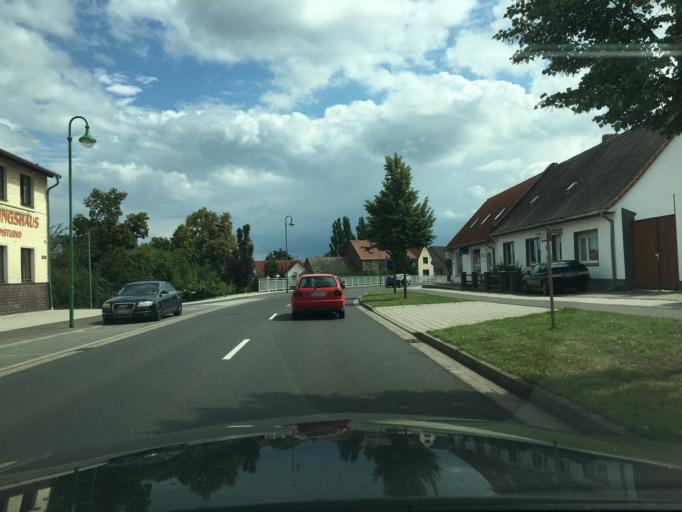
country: DE
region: Saxony-Anhalt
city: Bobbau
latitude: 51.6892
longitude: 12.2699
